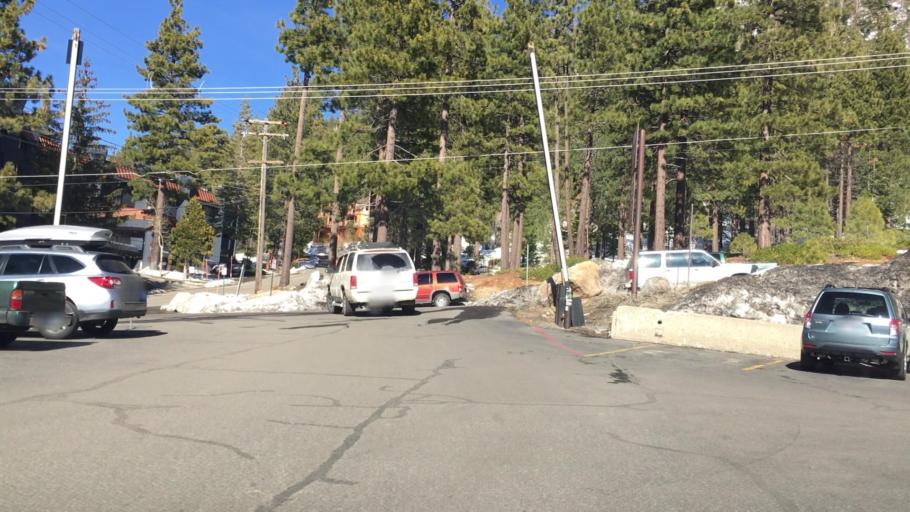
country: US
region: California
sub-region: El Dorado County
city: South Lake Tahoe
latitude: 38.9377
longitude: -119.9388
